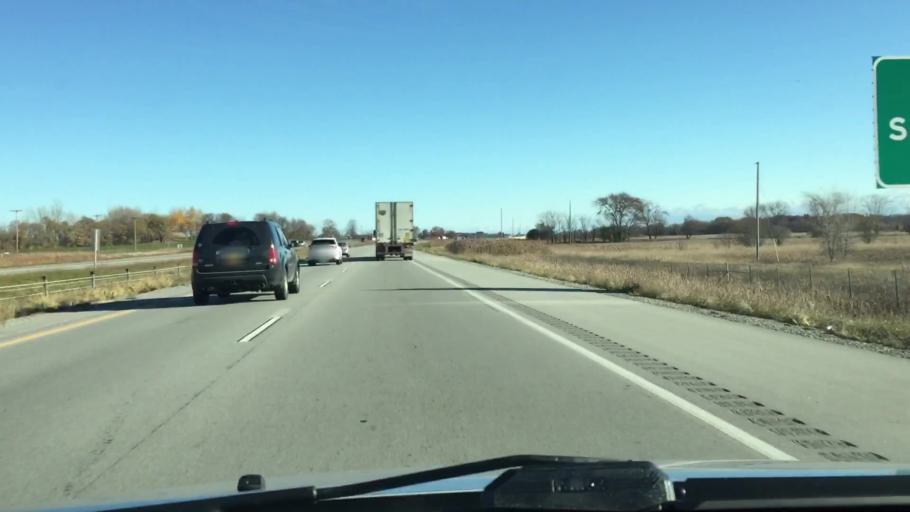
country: US
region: Wisconsin
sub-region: Brown County
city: De Pere
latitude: 44.4181
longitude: -88.1307
